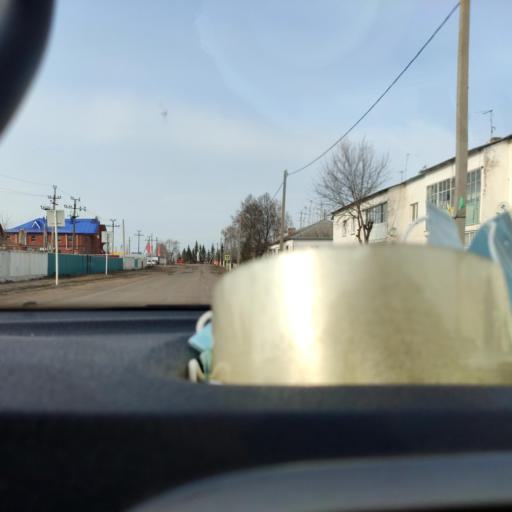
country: RU
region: Bashkortostan
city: Ulukulevo
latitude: 54.3770
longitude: 56.4496
